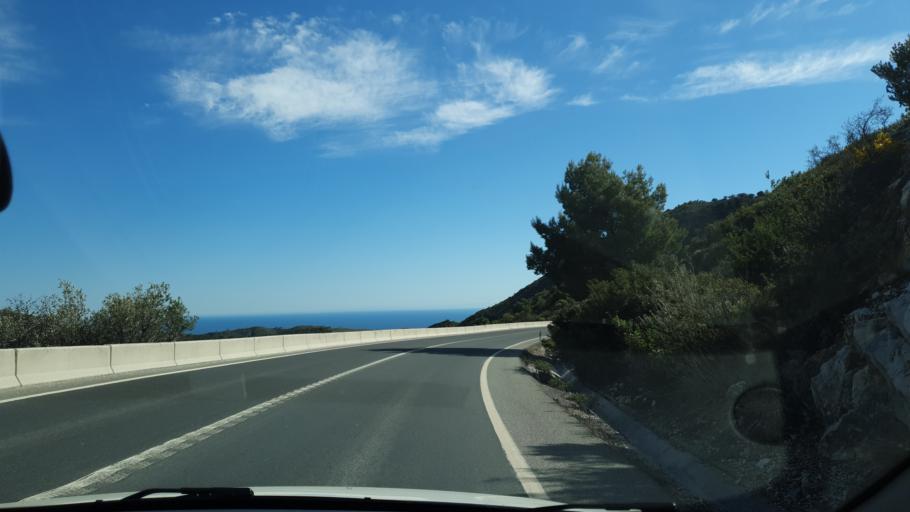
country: ES
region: Andalusia
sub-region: Provincia de Malaga
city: Ojen
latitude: 36.5789
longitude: -4.8530
